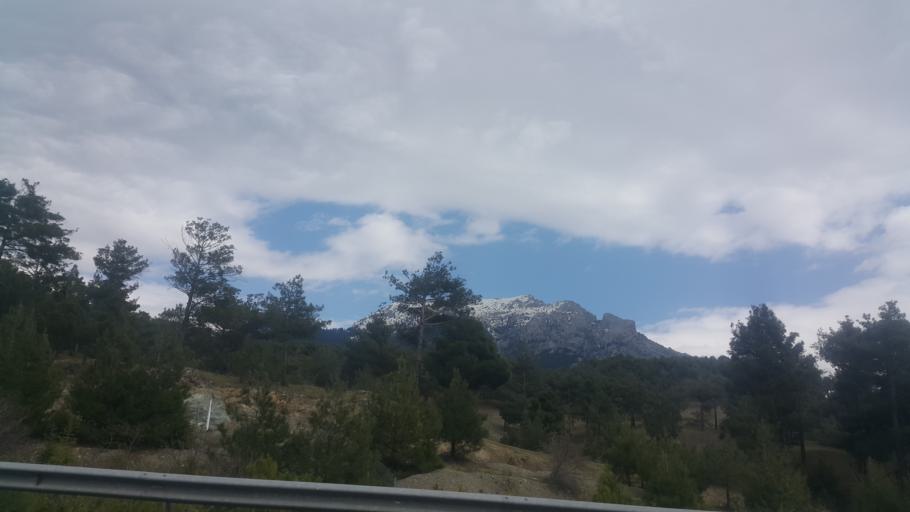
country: TR
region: Adana
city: Pozanti
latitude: 37.4311
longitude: 34.8811
